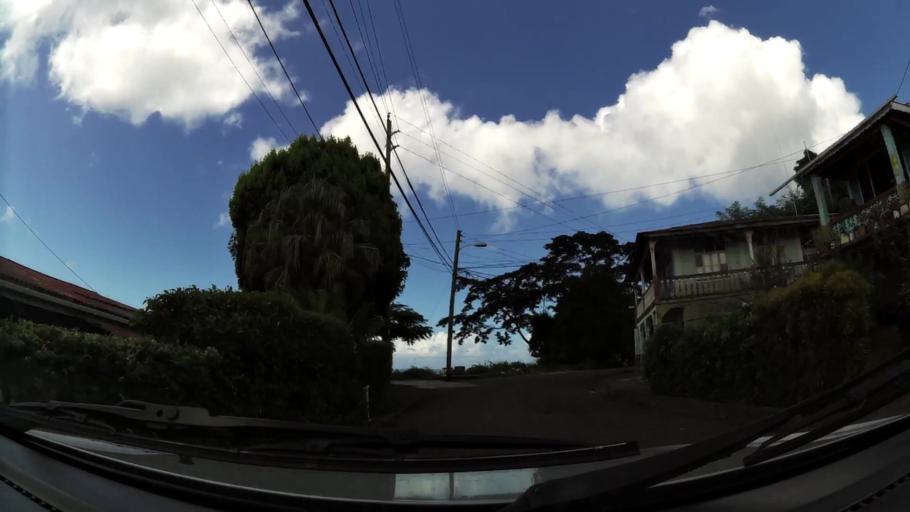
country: GD
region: Saint Mark
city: Victoria
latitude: 12.1825
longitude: -61.7237
